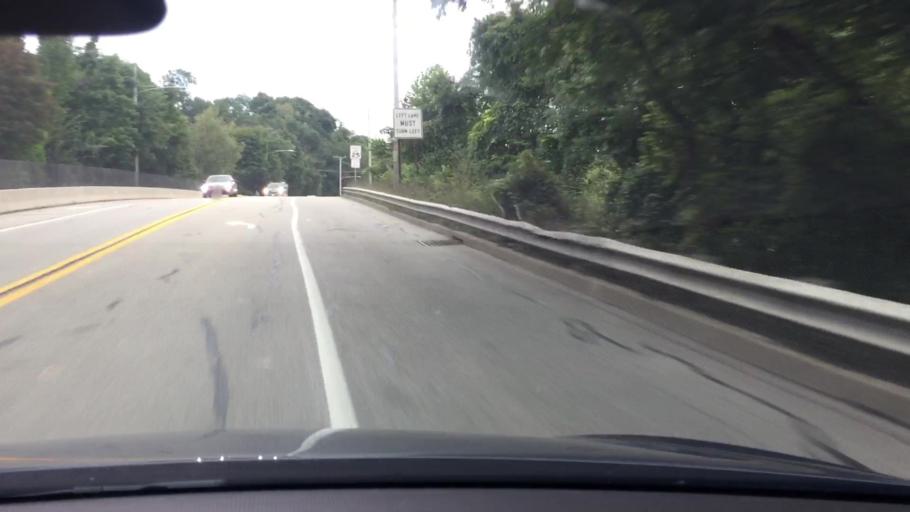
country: US
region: Pennsylvania
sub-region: Allegheny County
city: Verona
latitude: 40.5103
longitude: -79.8432
